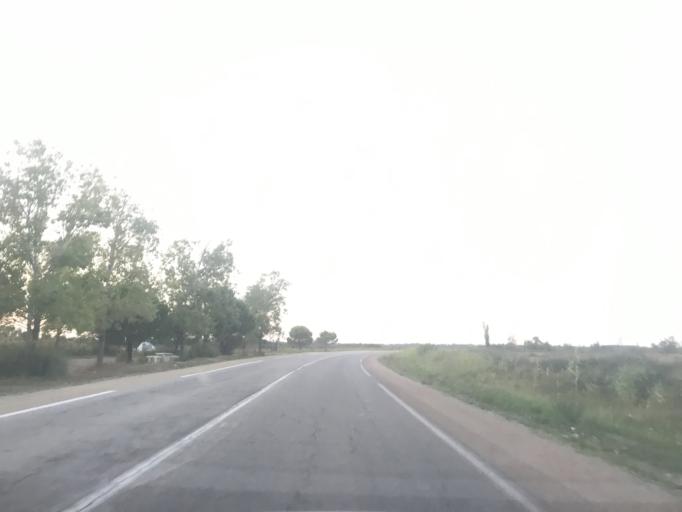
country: FR
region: Provence-Alpes-Cote d'Azur
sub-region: Departement des Bouches-du-Rhone
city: Saintes-Maries-de-la-Mer
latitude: 43.5297
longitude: 4.4009
